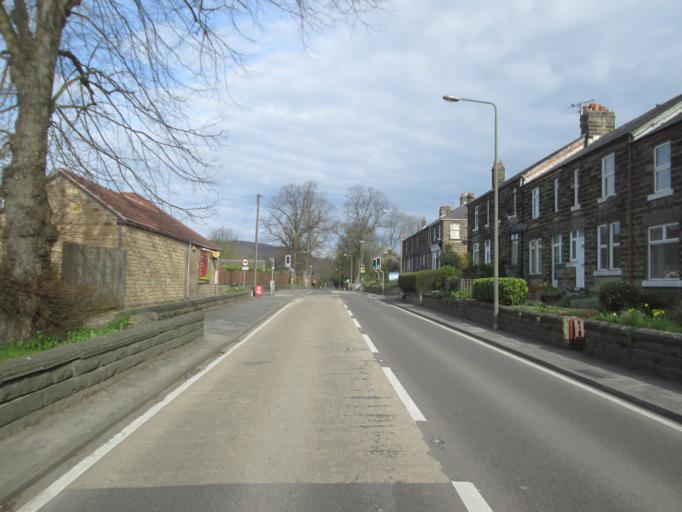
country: GB
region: England
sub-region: Derbyshire
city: Matlock
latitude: 53.1663
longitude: -1.5980
